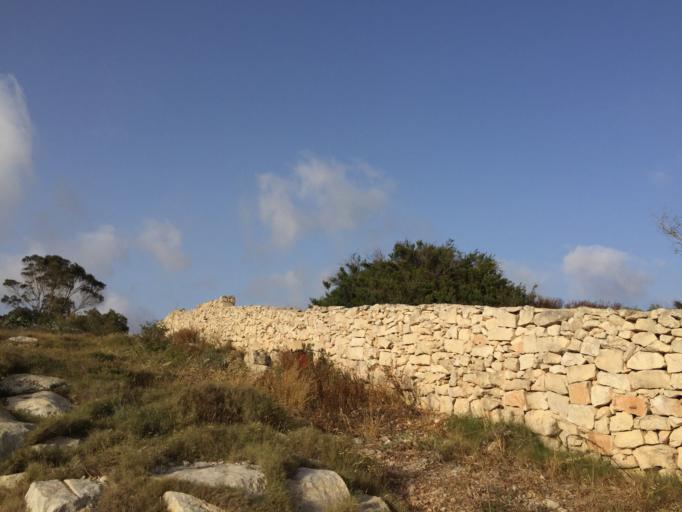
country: MT
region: Il-Qrendi
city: Qrendi
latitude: 35.8261
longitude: 14.4429
